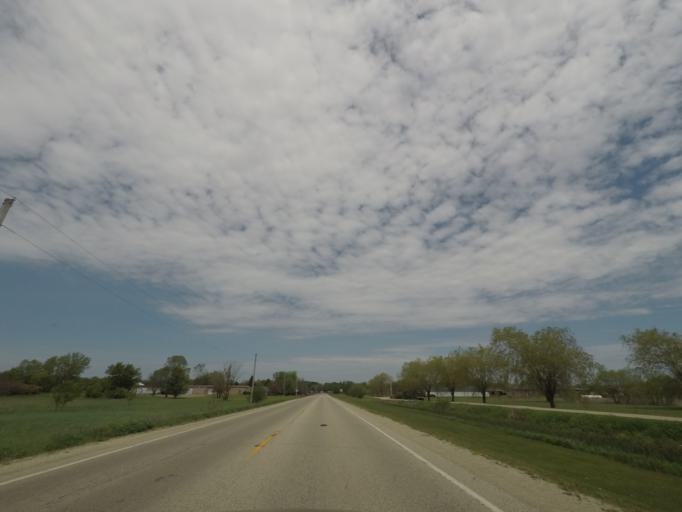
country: US
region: Wisconsin
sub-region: Rock County
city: Evansville
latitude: 42.7673
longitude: -89.2990
